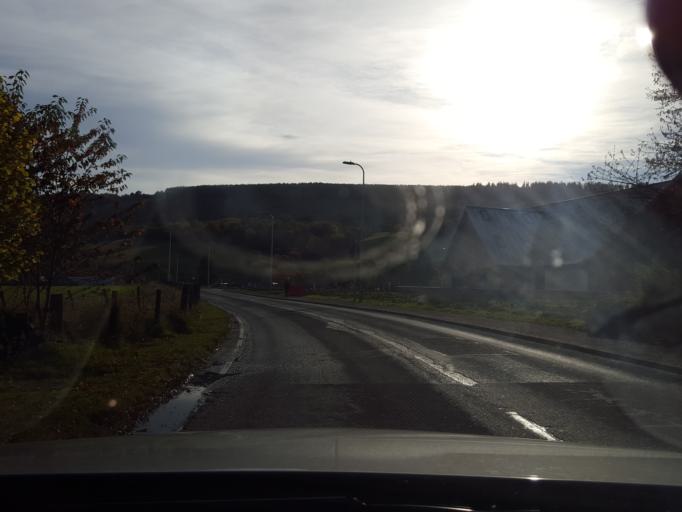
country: GB
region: Scotland
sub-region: Highland
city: Beauly
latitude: 57.3295
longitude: -4.4792
